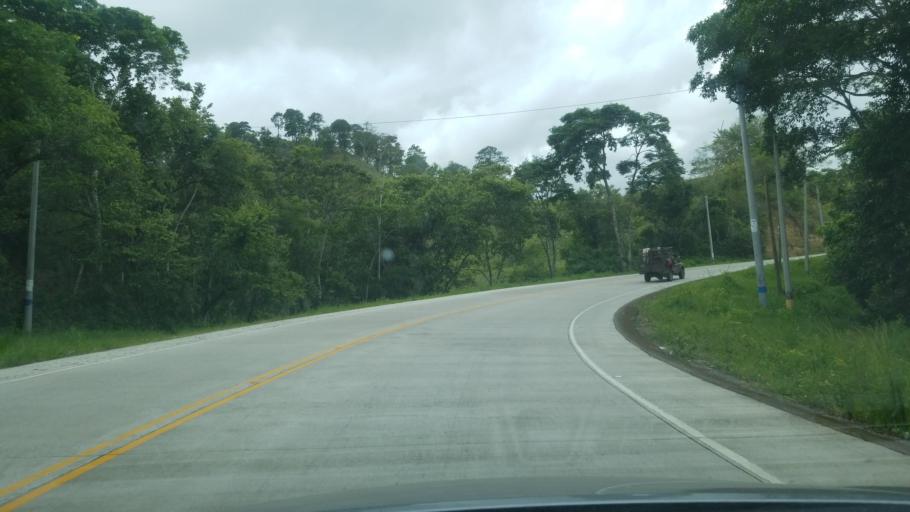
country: HN
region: Copan
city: San Jeronimo
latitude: 14.9814
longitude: -88.8743
